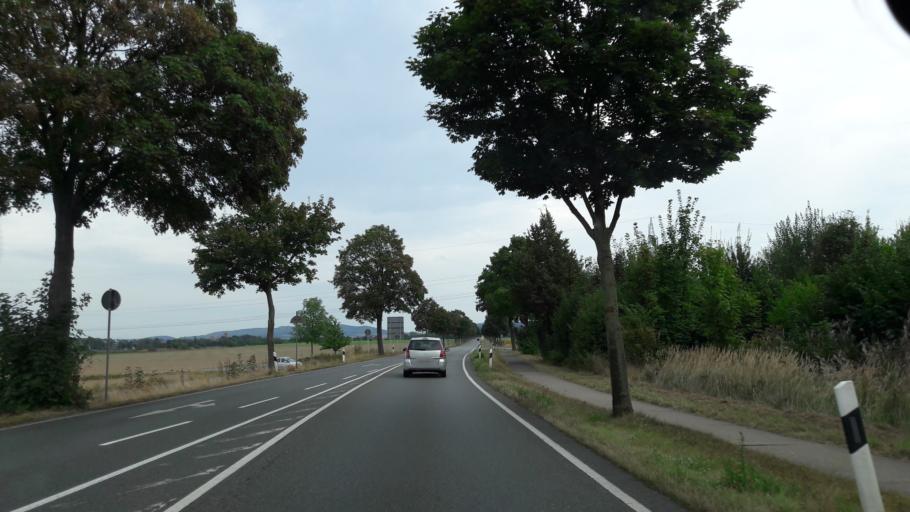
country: DE
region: Lower Saxony
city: Hildesheim
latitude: 52.1216
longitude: 9.9591
